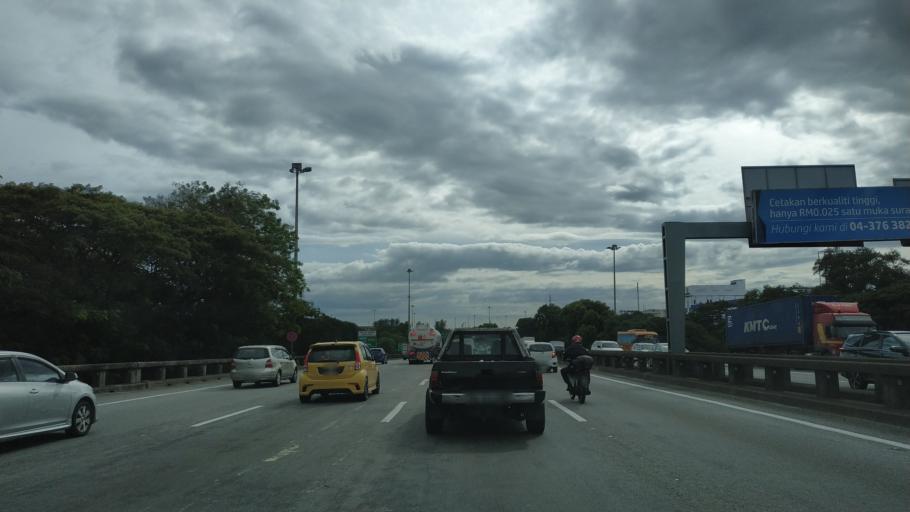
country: MY
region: Penang
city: Perai
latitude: 5.3724
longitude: 100.4011
